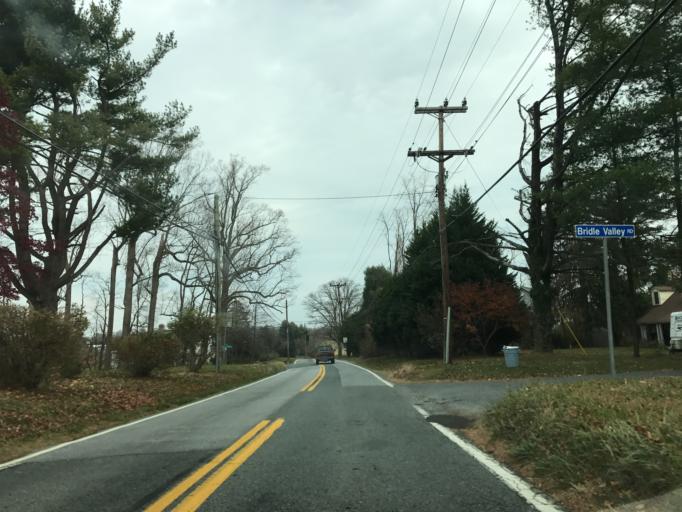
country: US
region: Maryland
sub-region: Baltimore County
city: Carney
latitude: 39.4489
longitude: -76.5329
